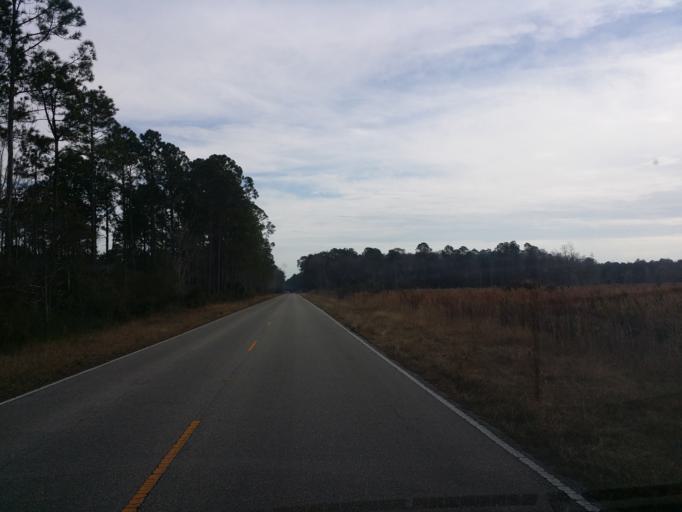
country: US
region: Florida
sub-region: Leon County
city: Woodville
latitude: 30.1668
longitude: -84.1571
